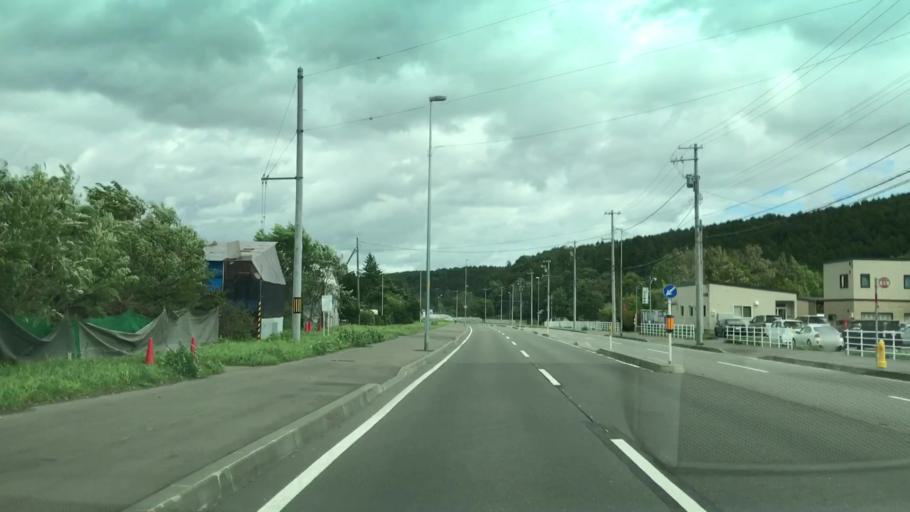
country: JP
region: Hokkaido
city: Kitahiroshima
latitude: 42.9534
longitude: 141.4518
